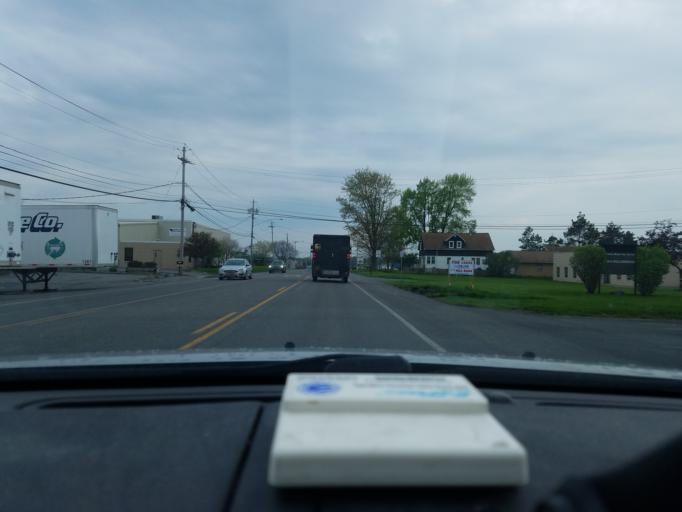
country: US
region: New York
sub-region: Onondaga County
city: East Syracuse
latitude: 43.0999
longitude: -76.0845
